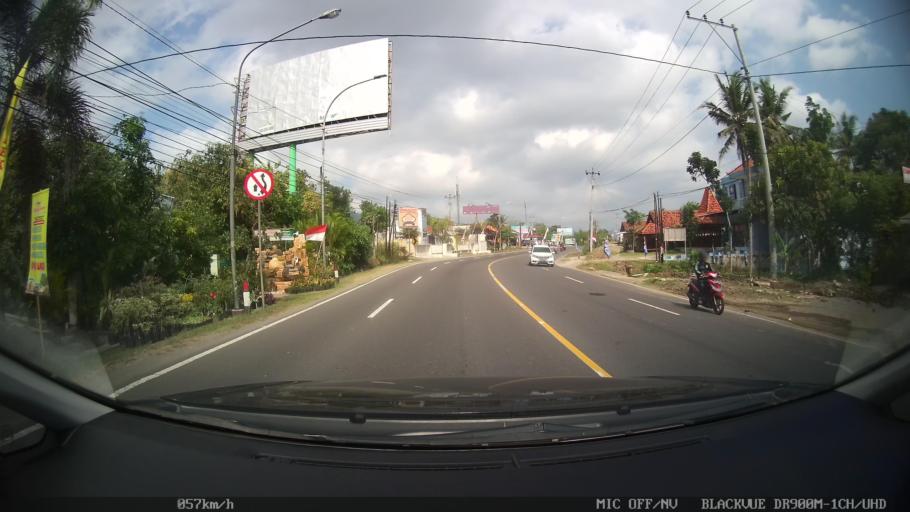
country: ID
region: Daerah Istimewa Yogyakarta
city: Srandakan
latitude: -7.8671
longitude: 110.1667
